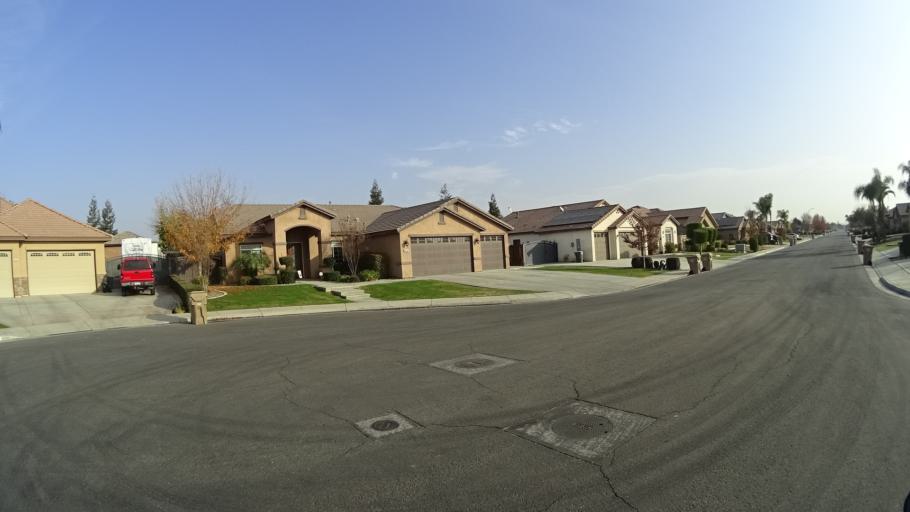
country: US
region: California
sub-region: Kern County
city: Greenacres
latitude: 35.4328
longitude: -119.1182
